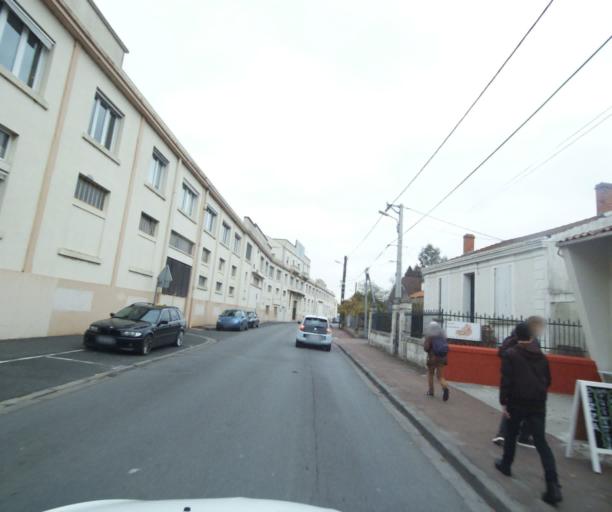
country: FR
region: Poitou-Charentes
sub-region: Departement de la Charente-Maritime
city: Saintes
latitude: 45.7395
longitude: -0.6188
